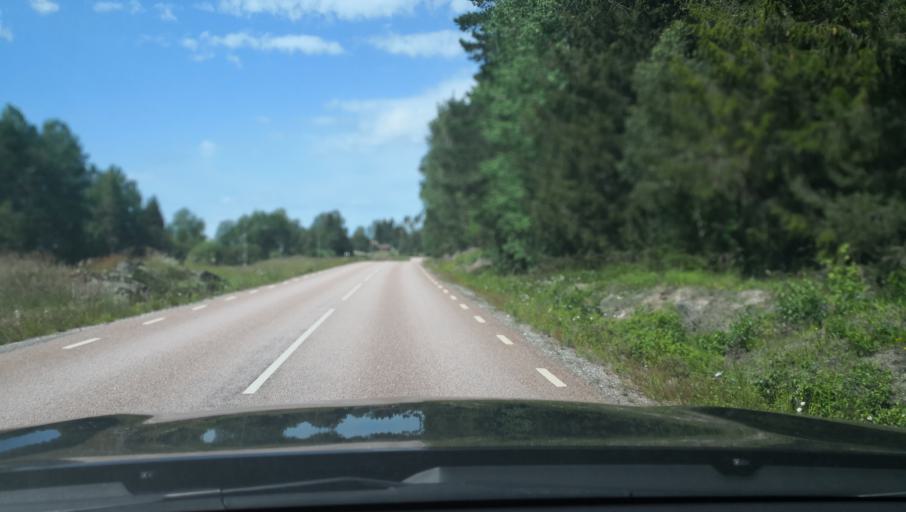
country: SE
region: Vaestmanland
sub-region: Surahammars Kommun
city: Ramnas
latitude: 59.8530
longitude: 16.0965
